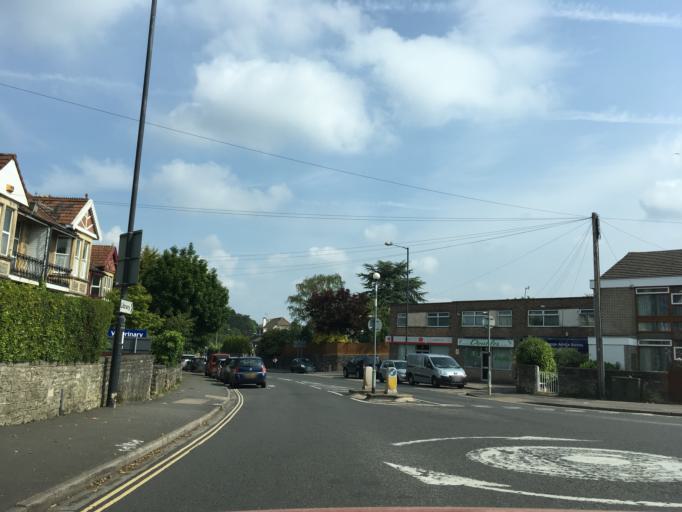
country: GB
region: England
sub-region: North Somerset
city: Dundry
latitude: 51.4163
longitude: -2.6176
